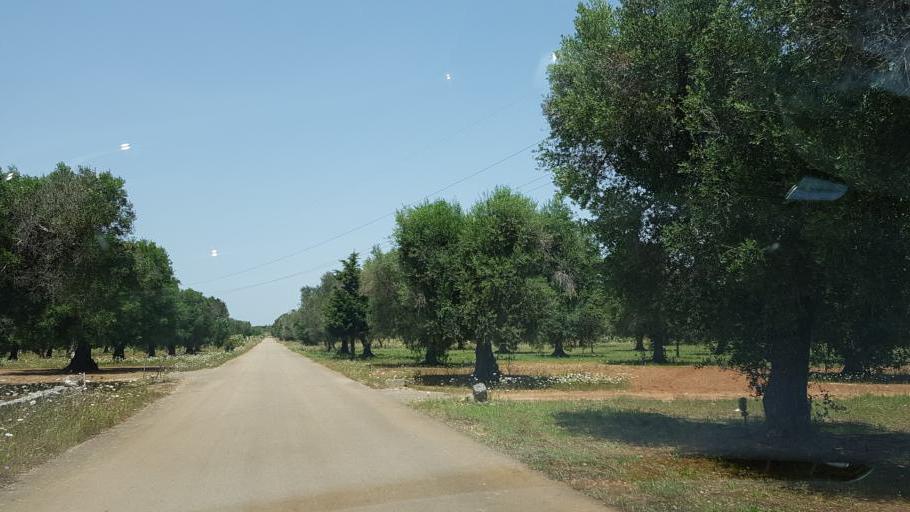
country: IT
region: Apulia
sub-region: Provincia di Lecce
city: Porto Cesareo
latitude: 40.3198
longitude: 17.8943
